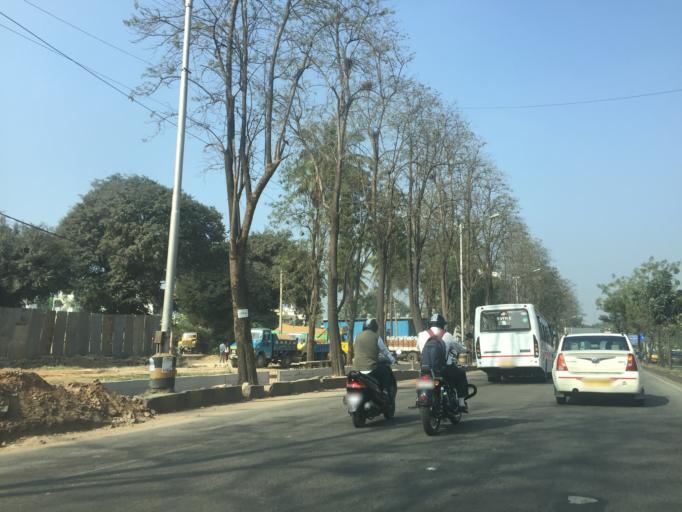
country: IN
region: Karnataka
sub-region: Bangalore Urban
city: Yelahanka
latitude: 13.0419
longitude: 77.5961
